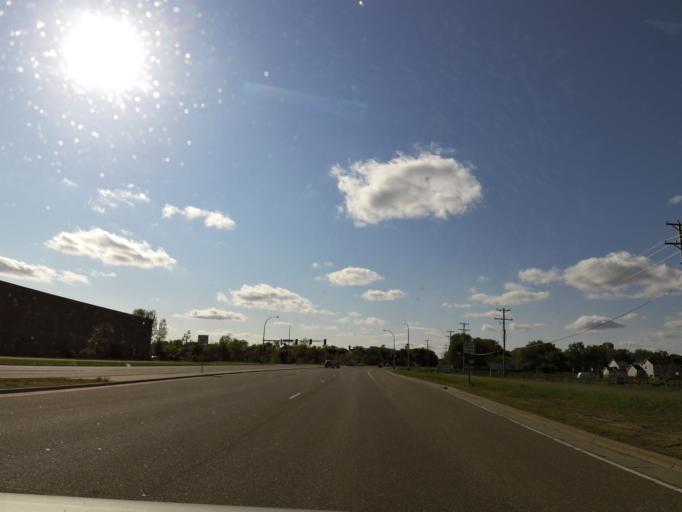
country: US
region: Minnesota
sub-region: Scott County
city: Prior Lake
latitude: 44.7065
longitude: -93.4102
